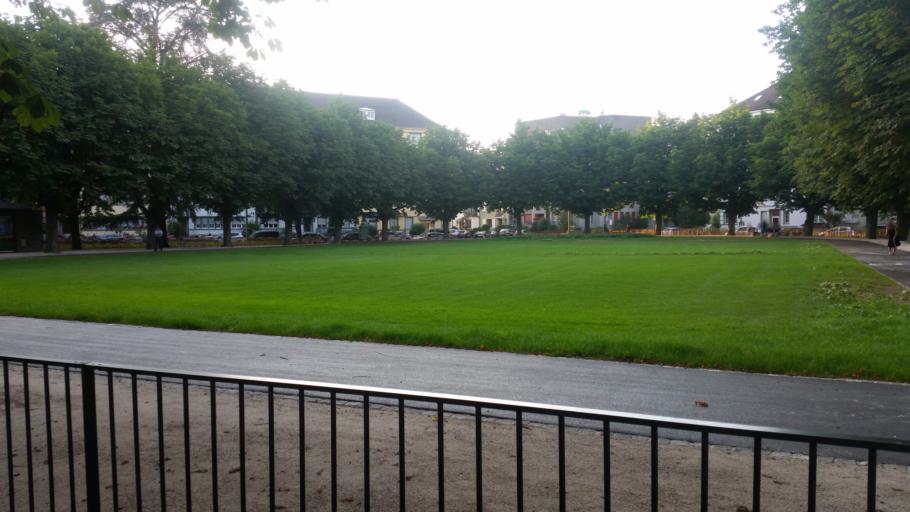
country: CH
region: Basel-City
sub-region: Basel-Stadt
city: Basel
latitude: 47.5574
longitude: 7.5699
